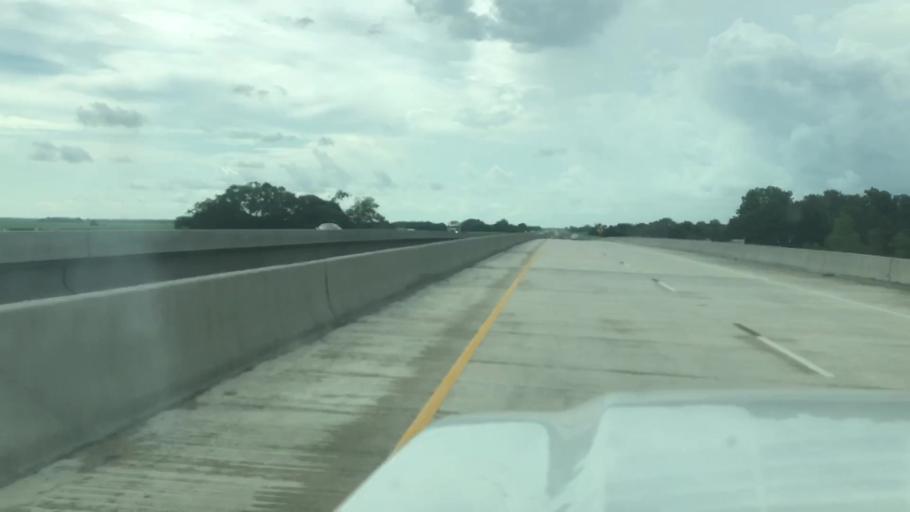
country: US
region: Louisiana
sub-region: Iberia Parish
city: Jeanerette
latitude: 29.8665
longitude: -91.6332
